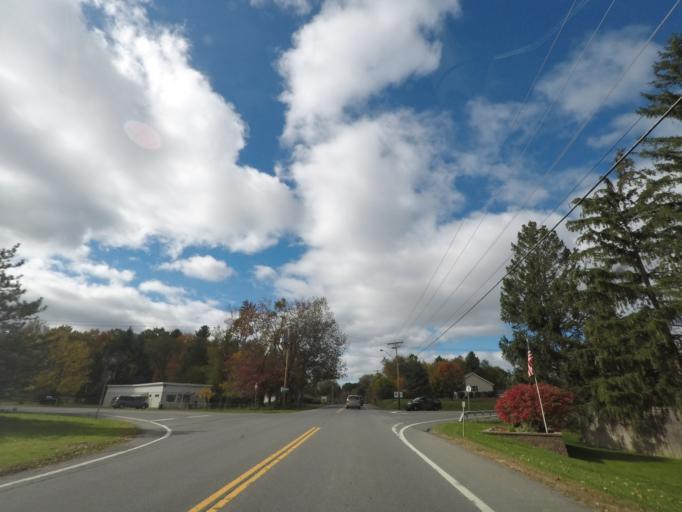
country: US
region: New York
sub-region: Albany County
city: Cohoes
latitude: 42.8229
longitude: -73.7423
